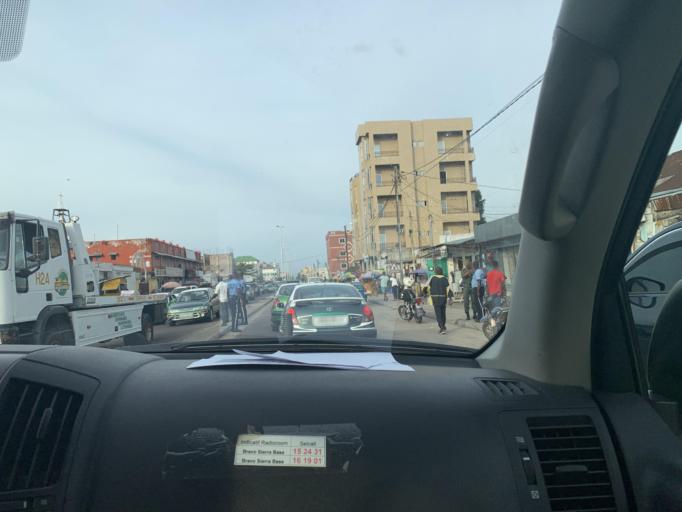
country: CG
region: Brazzaville
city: Brazzaville
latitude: -4.2540
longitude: 15.2739
